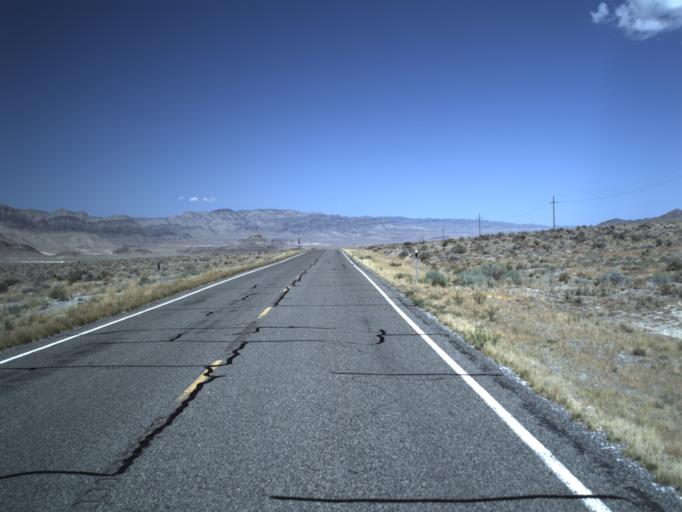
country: US
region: Utah
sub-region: Beaver County
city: Milford
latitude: 39.0259
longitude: -113.3731
